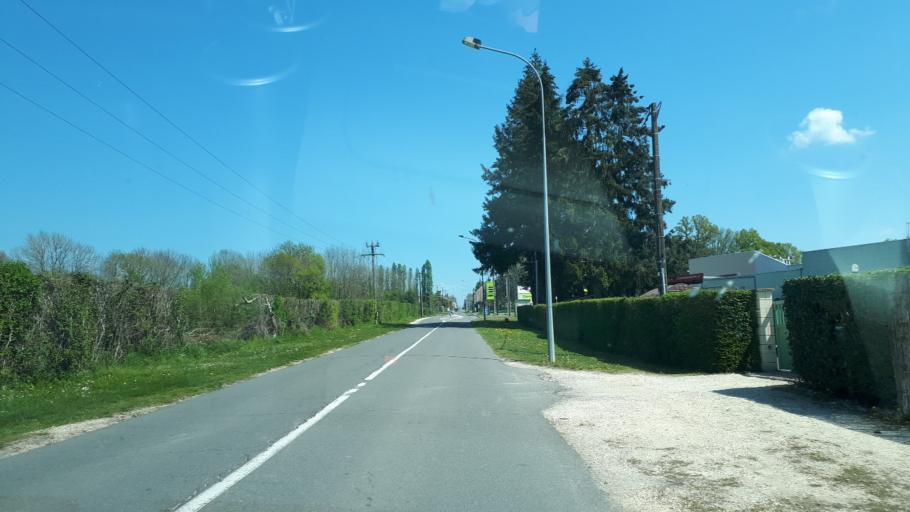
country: FR
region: Centre
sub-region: Departement du Cher
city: Henrichemont
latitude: 47.2989
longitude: 2.5149
